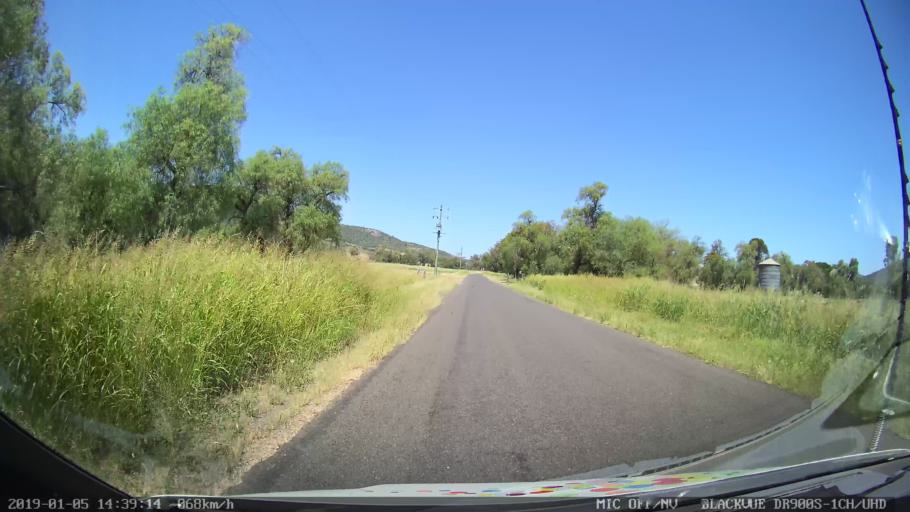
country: AU
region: New South Wales
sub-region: Tamworth Municipality
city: Phillip
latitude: -31.2541
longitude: 150.6976
